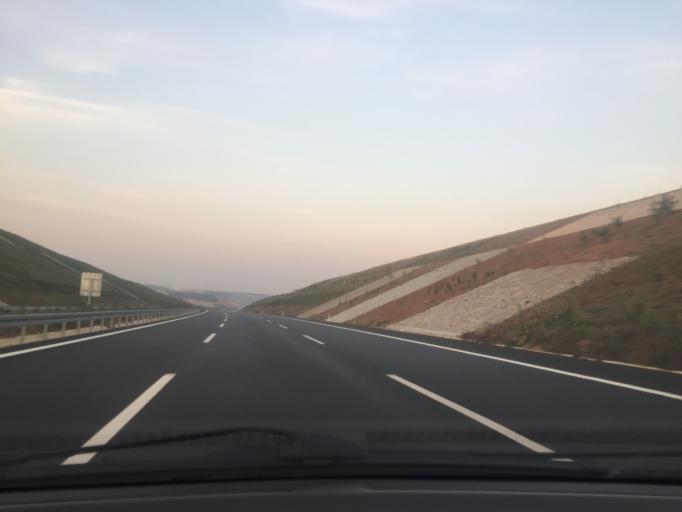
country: TR
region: Bursa
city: Mahmudiye
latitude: 40.2774
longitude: 28.5357
